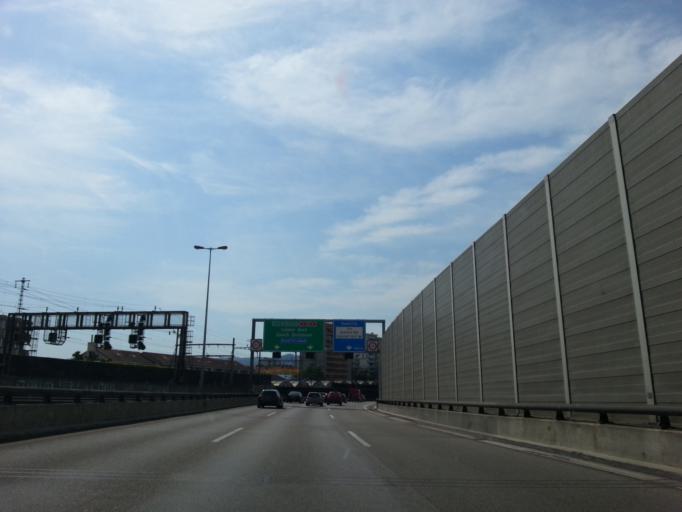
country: CH
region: Basel-Landschaft
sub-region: Bezirk Arlesheim
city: Birsfelden
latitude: 47.5546
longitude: 7.6158
